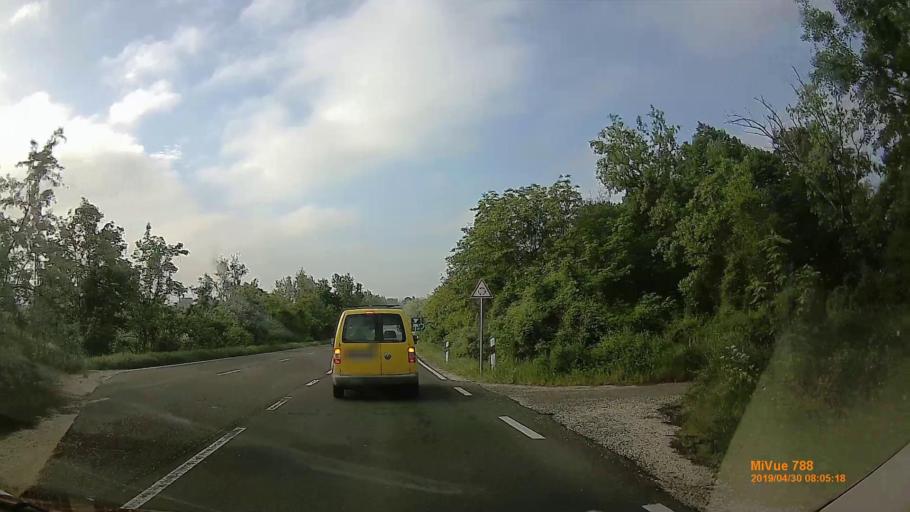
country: HU
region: Pest
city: Dunabogdany
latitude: 47.8168
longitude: 19.0919
